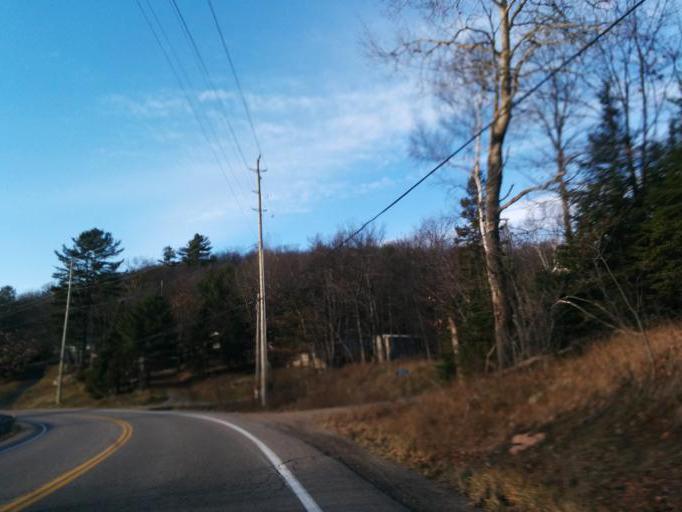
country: CA
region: Ontario
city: Bancroft
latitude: 45.0224
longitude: -78.3657
